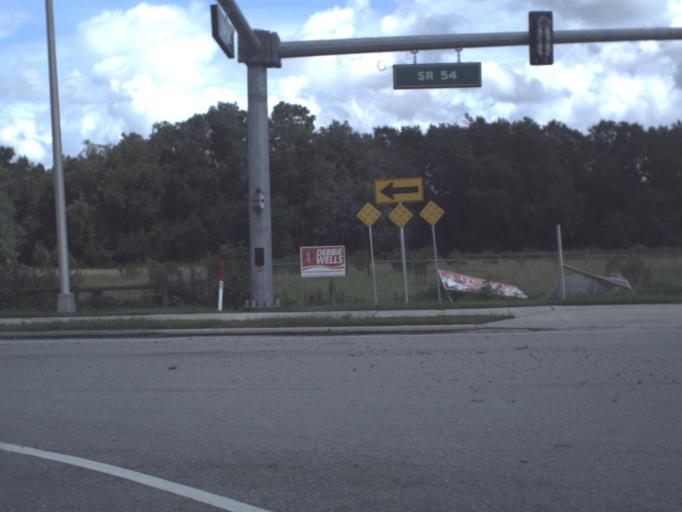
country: US
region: Florida
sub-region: Pasco County
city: Wesley Chapel
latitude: 28.2375
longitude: -82.3053
